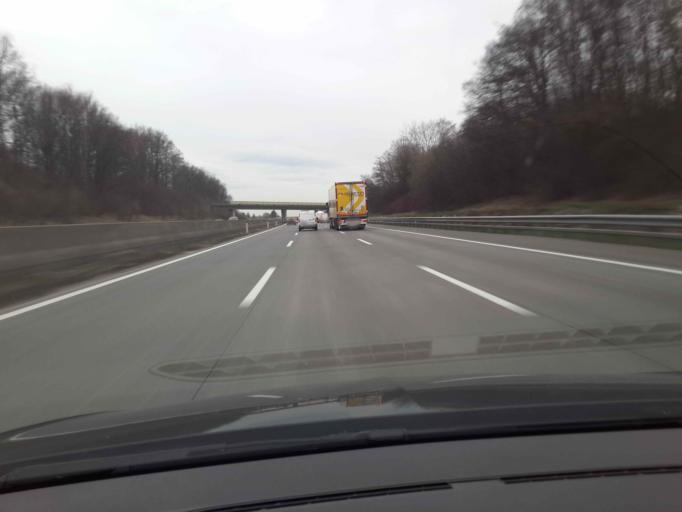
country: AT
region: Lower Austria
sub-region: Politischer Bezirk Amstetten
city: Amstetten
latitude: 48.1472
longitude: 14.9020
